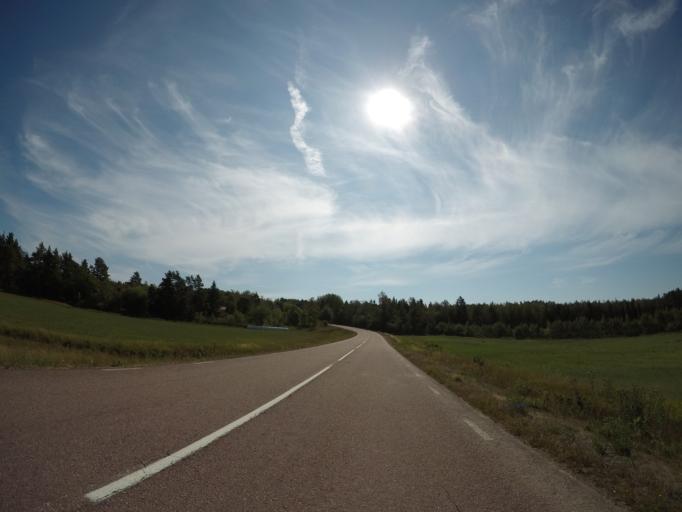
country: AX
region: Alands landsbygd
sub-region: Finstroem
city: Finstroem
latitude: 60.2756
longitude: 19.9112
